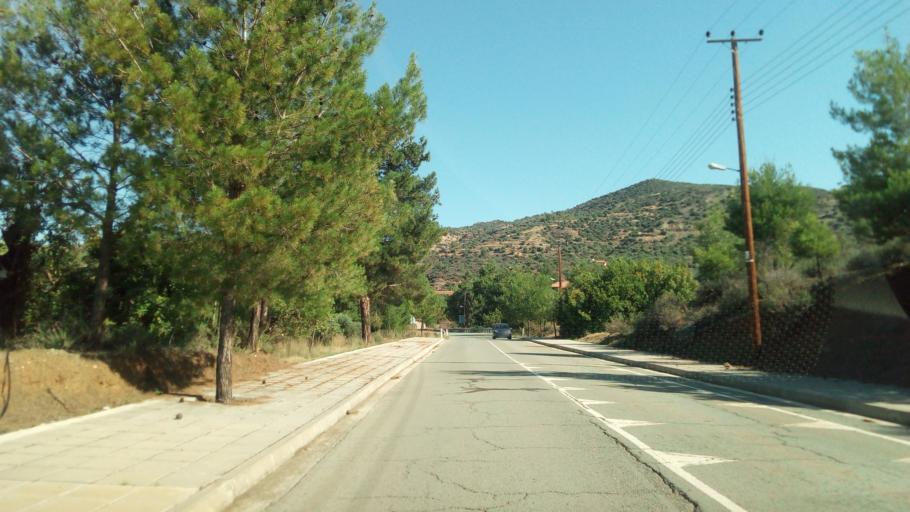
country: CY
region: Lefkosia
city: Lythrodontas
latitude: 34.8452
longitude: 33.2464
